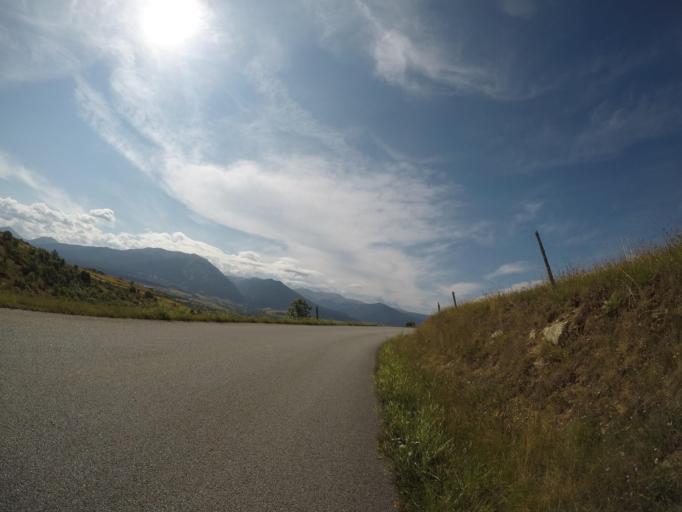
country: ES
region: Catalonia
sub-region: Provincia de Girona
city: Llivia
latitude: 42.4987
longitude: 2.0559
